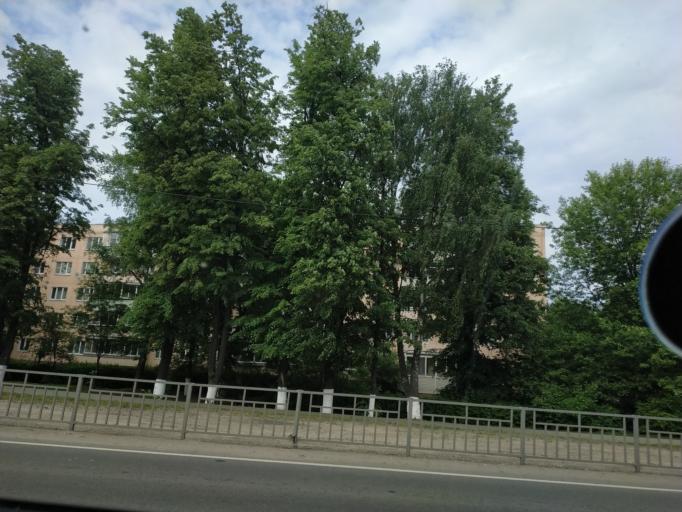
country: RU
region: Moskovskaya
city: Bronnitsy
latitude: 55.4164
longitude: 38.2821
